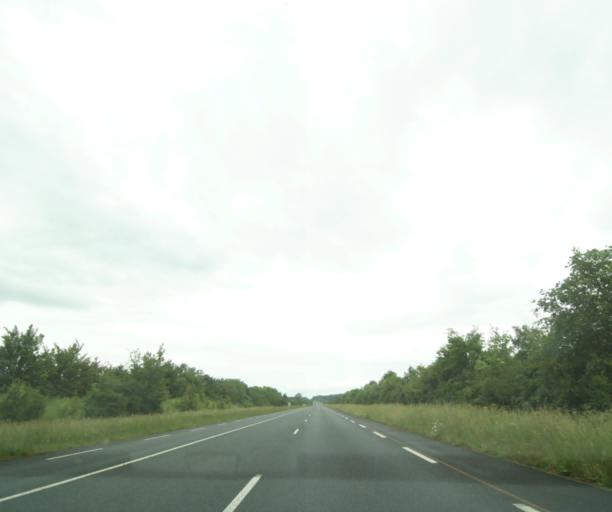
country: FR
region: Poitou-Charentes
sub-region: Departement des Deux-Sevres
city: Airvault
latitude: 46.7802
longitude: -0.2179
